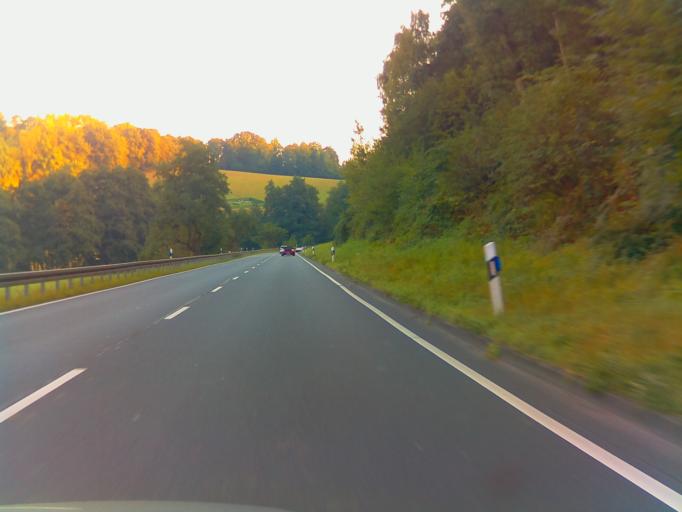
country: DE
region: Hesse
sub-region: Regierungsbezirk Darmstadt
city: Beerfelden
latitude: 49.6124
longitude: 8.9920
